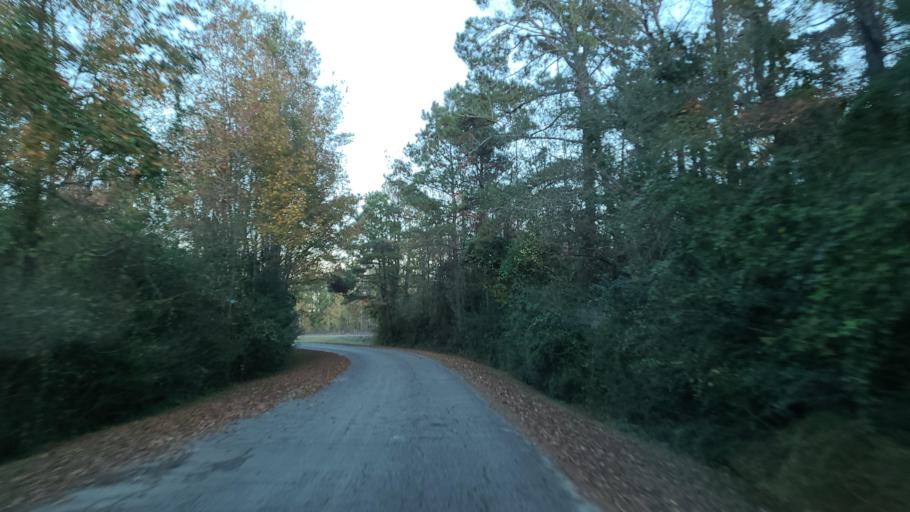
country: US
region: Mississippi
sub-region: Stone County
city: Wiggins
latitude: 31.0547
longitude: -89.1906
